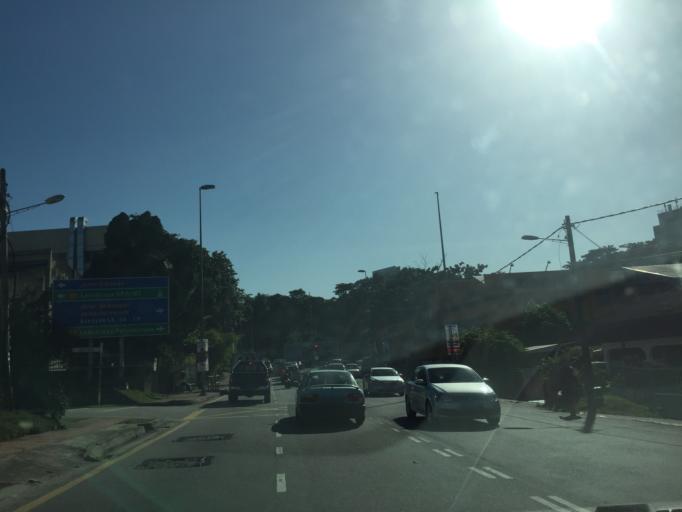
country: MY
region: Selangor
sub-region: Petaling
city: Petaling Jaya
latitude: 3.1190
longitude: 101.6283
